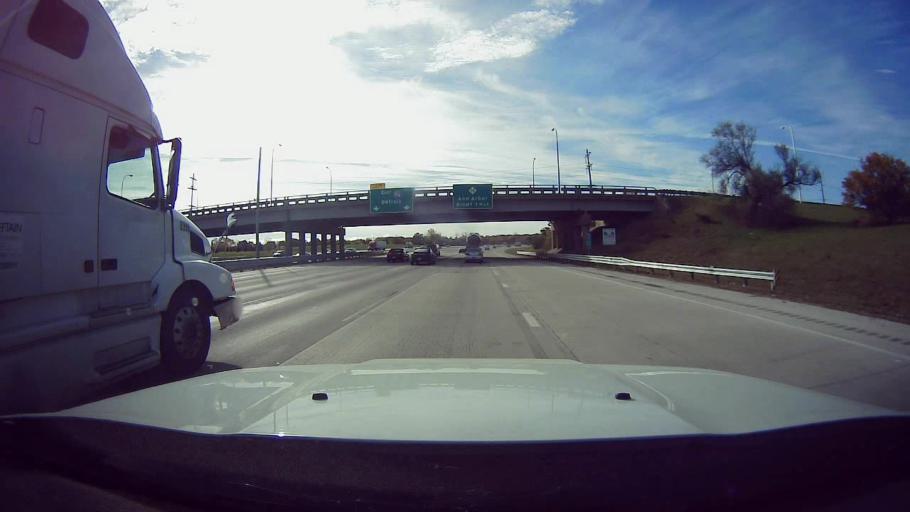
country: US
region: Michigan
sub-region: Wayne County
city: Plymouth
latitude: 42.4112
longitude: -83.4241
